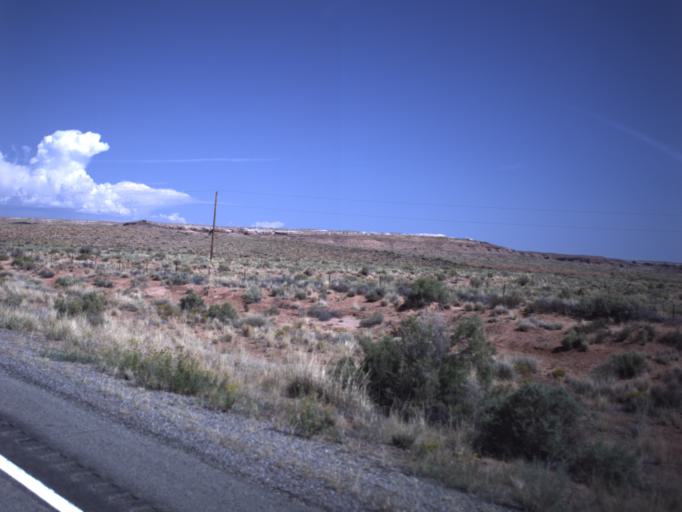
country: US
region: Utah
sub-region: San Juan County
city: Blanding
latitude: 37.1222
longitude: -109.5451
